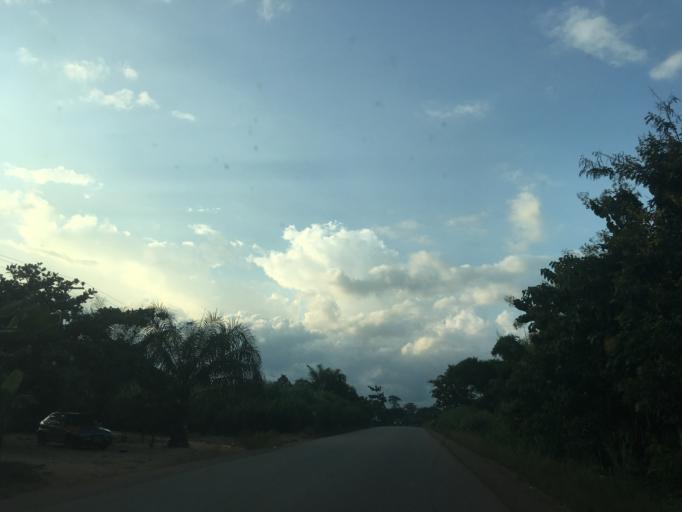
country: GH
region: Western
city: Bibiani
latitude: 6.6554
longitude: -2.4262
